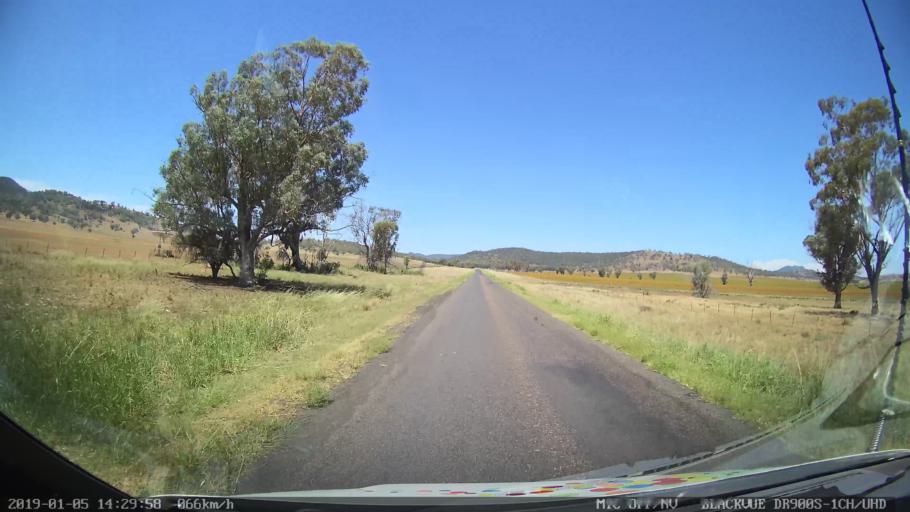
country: AU
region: New South Wales
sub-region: Tamworth Municipality
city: Phillip
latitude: -31.2281
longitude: 150.5867
